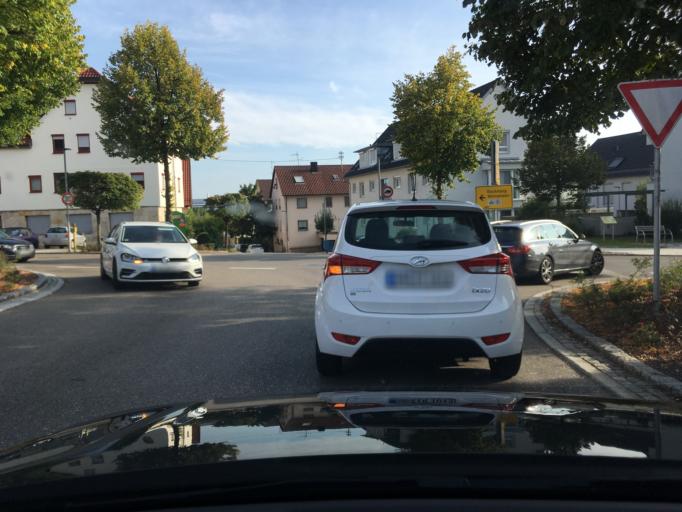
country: DE
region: Baden-Wuerttemberg
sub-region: Regierungsbezirk Stuttgart
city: Affalterbach
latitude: 48.9231
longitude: 9.3234
